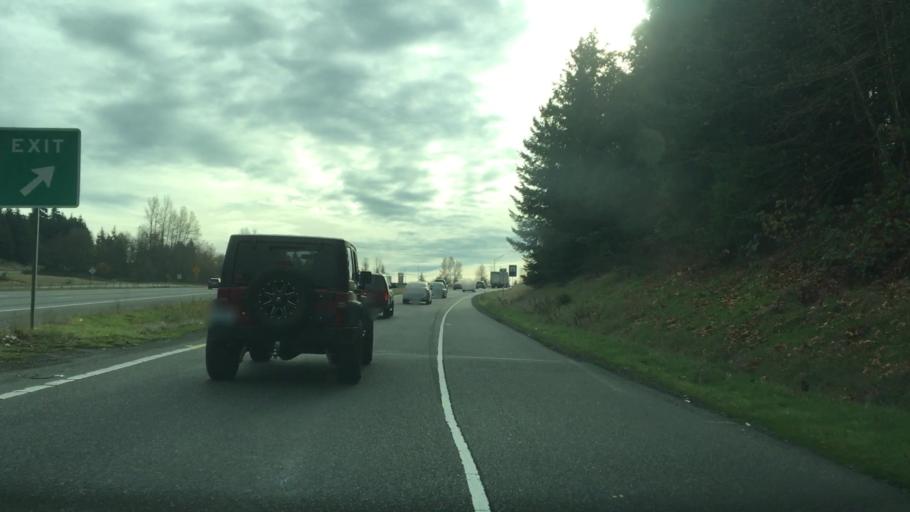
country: US
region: Washington
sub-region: Pierce County
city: Puyallup
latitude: 47.1659
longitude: -122.2971
